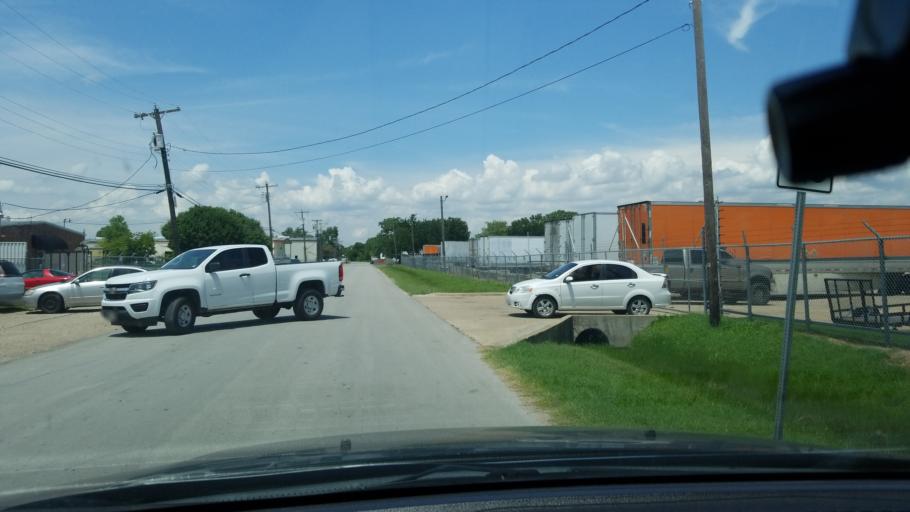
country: US
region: Texas
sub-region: Dallas County
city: Balch Springs
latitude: 32.7448
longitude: -96.6316
